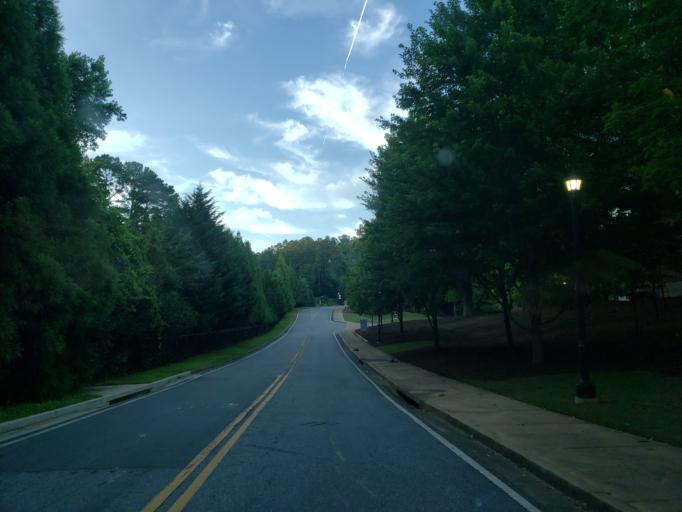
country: US
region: Georgia
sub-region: Cobb County
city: Kennesaw
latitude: 34.0384
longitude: -84.5864
